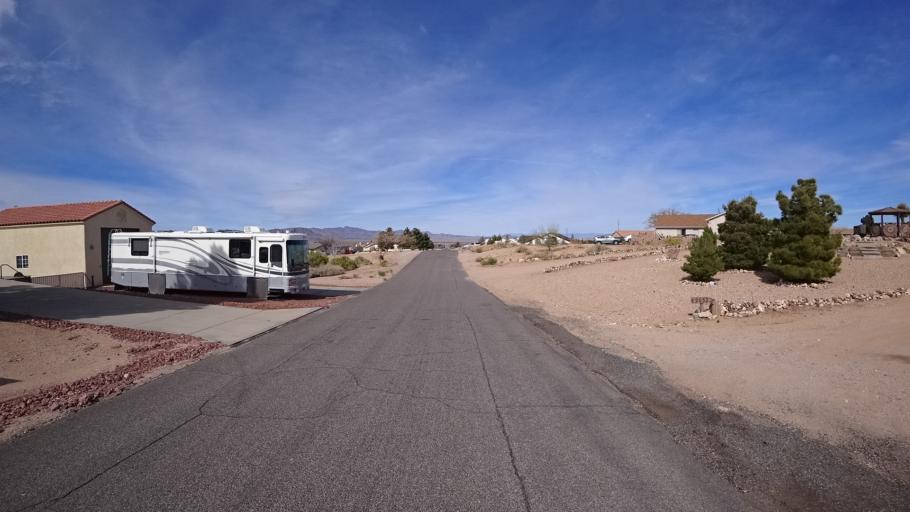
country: US
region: Arizona
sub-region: Mohave County
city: Kingman
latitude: 35.1827
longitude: -113.9844
